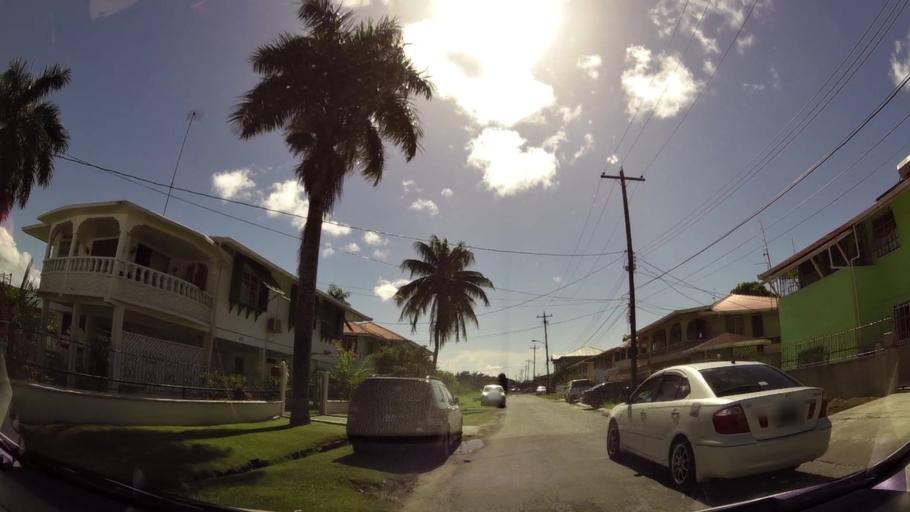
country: GY
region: Demerara-Mahaica
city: Georgetown
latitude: 6.8088
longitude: -58.1416
